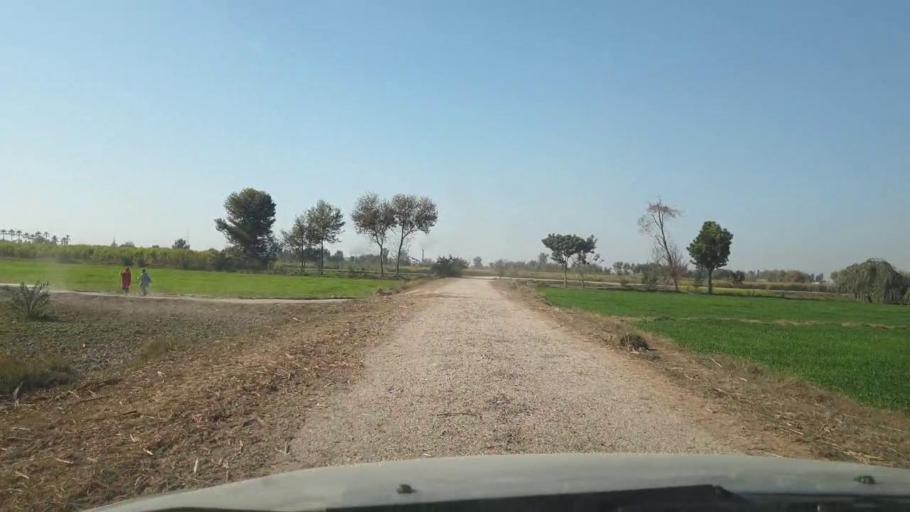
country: PK
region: Sindh
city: Ghotki
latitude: 28.0421
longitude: 69.3362
